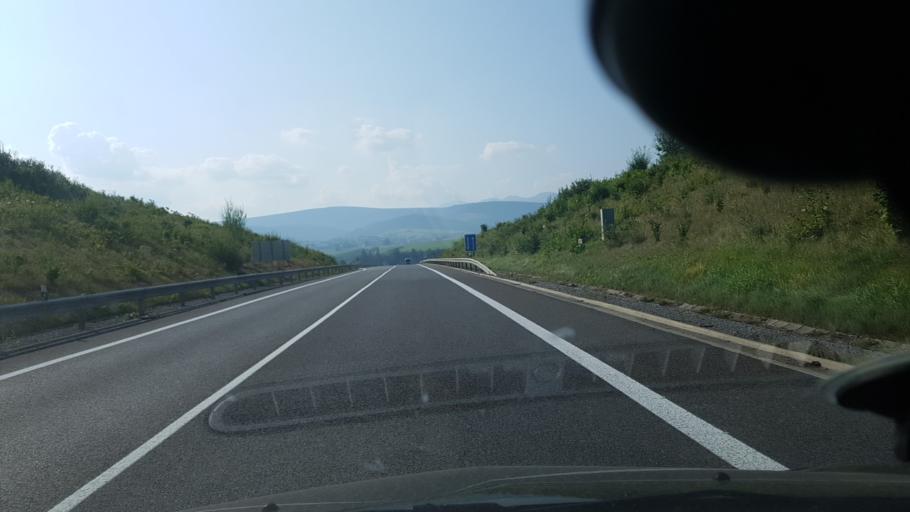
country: SK
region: Zilinsky
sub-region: Okres Zilina
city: Trstena
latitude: 49.3674
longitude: 19.6318
